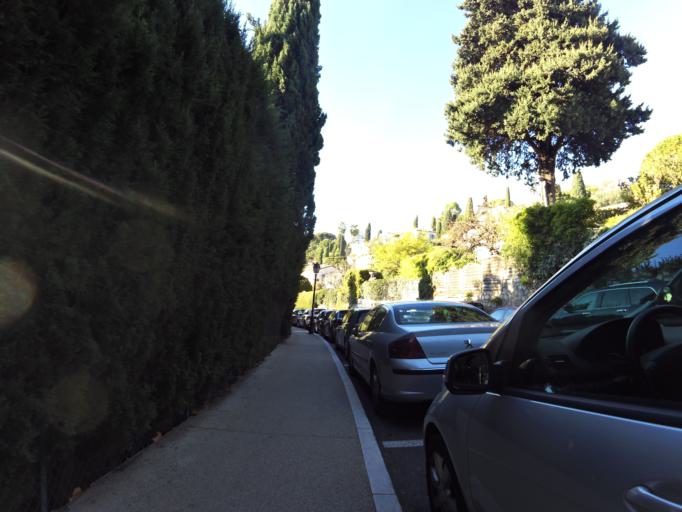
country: FR
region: Provence-Alpes-Cote d'Azur
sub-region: Departement des Alpes-Maritimes
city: Saint-Paul-de-Vence
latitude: 43.6988
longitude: 7.1215
